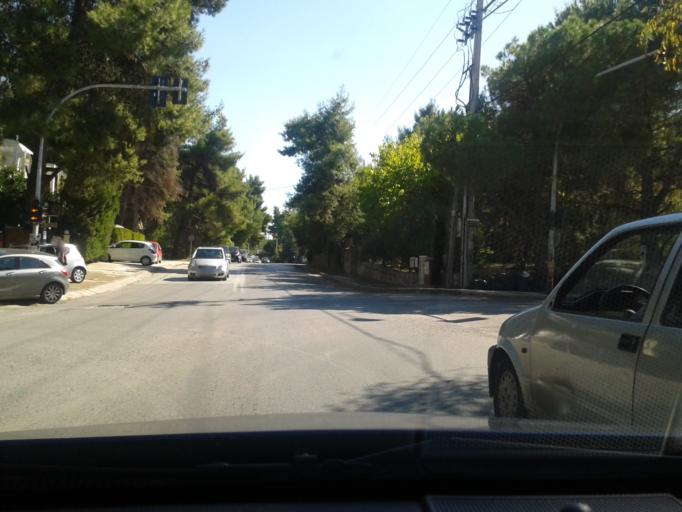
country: GR
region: Attica
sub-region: Nomarchia Anatolikis Attikis
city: Drosia
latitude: 38.1062
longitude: 23.8652
